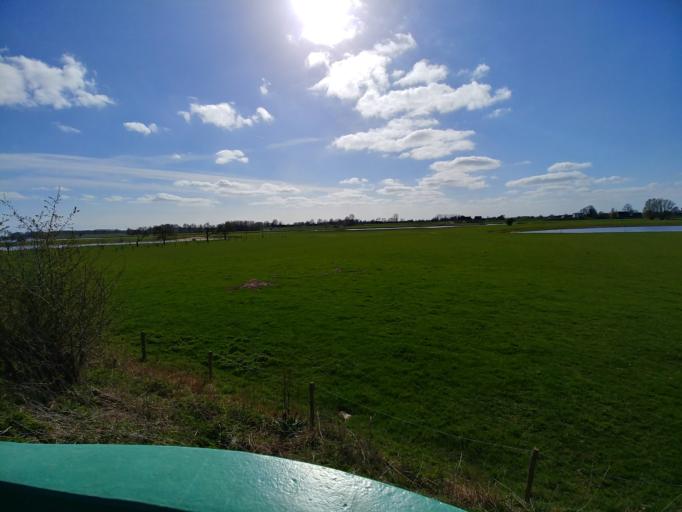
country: NL
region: Gelderland
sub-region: Gemeente Voorst
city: Twello
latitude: 52.2765
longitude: 6.1216
